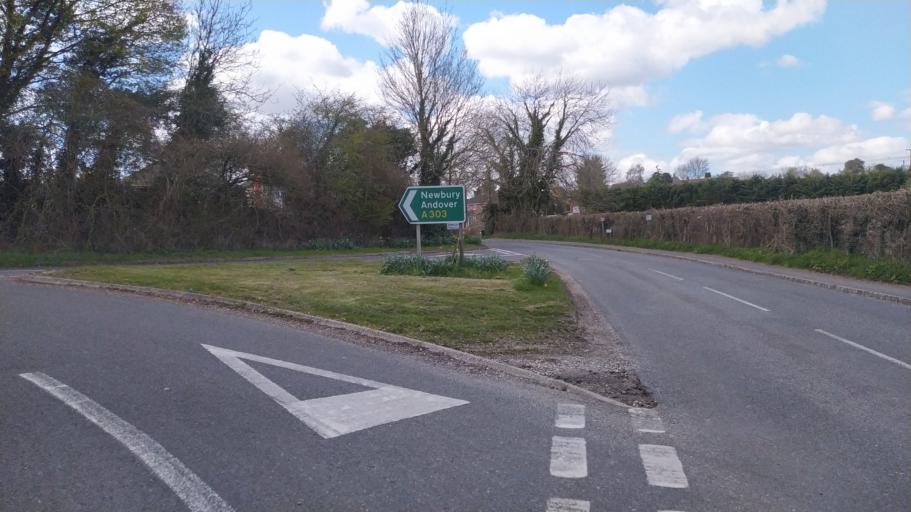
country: GB
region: England
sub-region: Hampshire
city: Abbotts Ann
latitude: 51.2102
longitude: -1.5792
